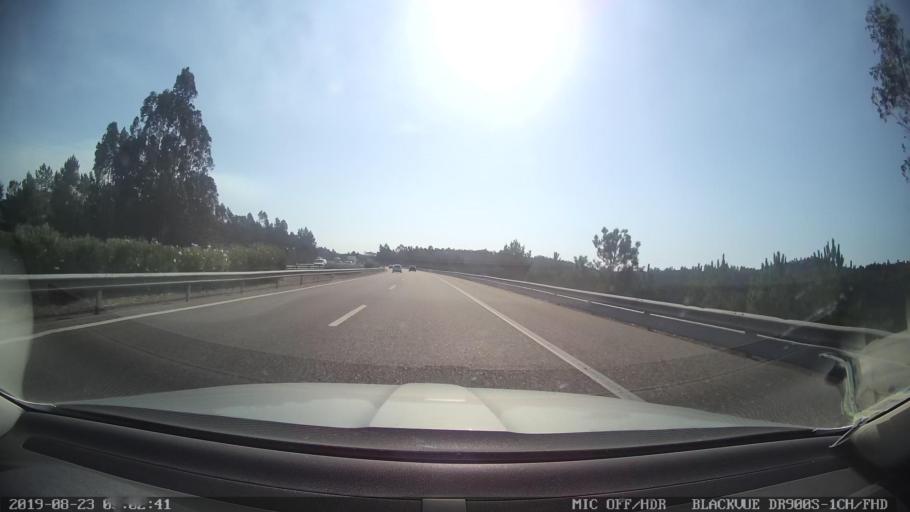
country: PT
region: Leiria
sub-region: Pombal
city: Pombal
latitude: 39.9691
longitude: -8.6544
